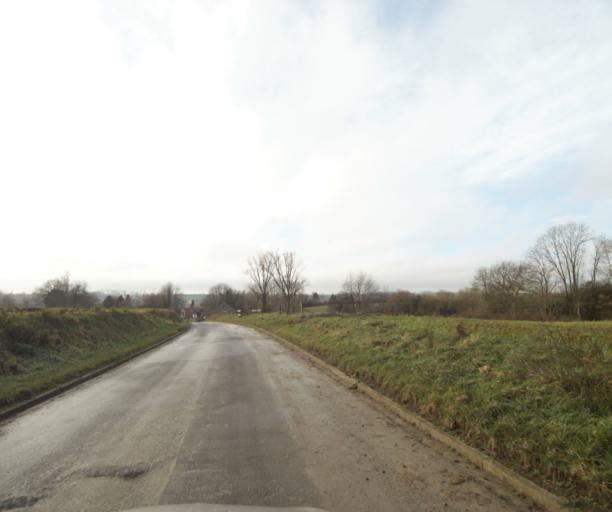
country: FR
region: Nord-Pas-de-Calais
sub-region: Departement du Nord
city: Vendegies-sur-Ecaillon
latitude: 50.2742
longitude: 3.4842
